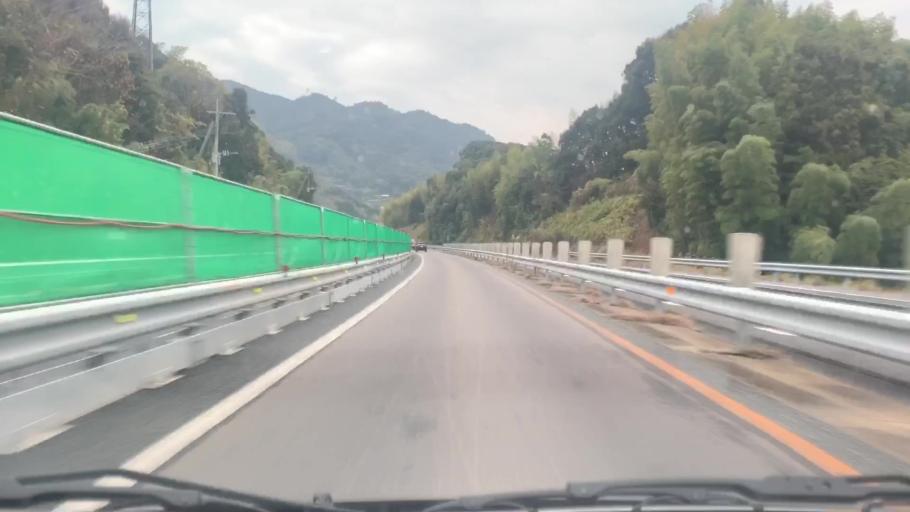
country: JP
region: Nagasaki
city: Obita
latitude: 32.8043
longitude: 129.9663
